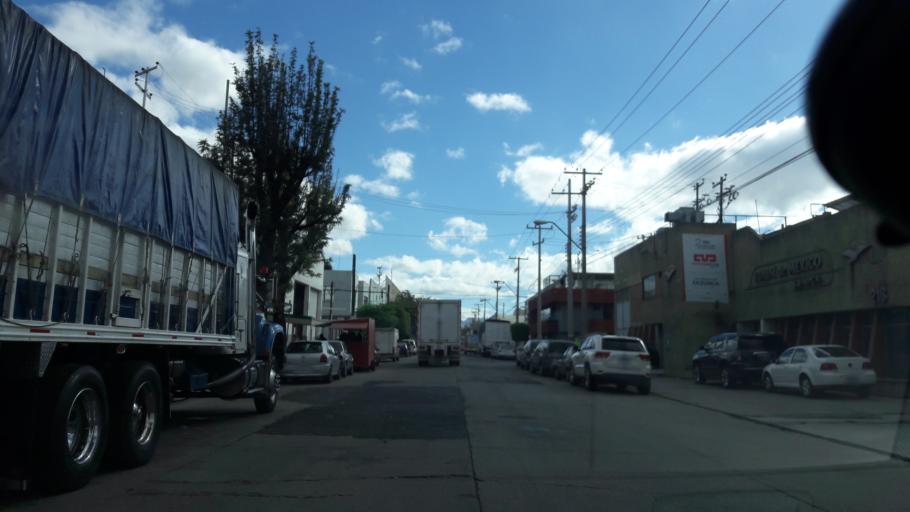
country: MX
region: Guanajuato
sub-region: Leon
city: Medina
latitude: 21.1026
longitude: -101.6315
